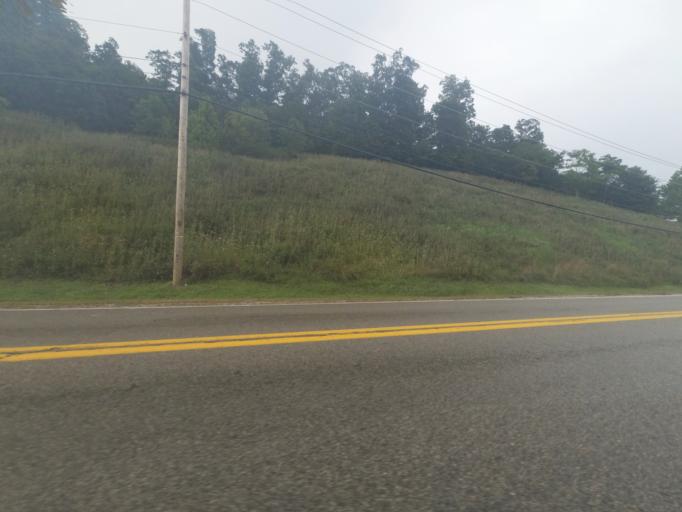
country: US
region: West Virginia
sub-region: Cabell County
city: Huntington
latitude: 38.3887
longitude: -82.3954
